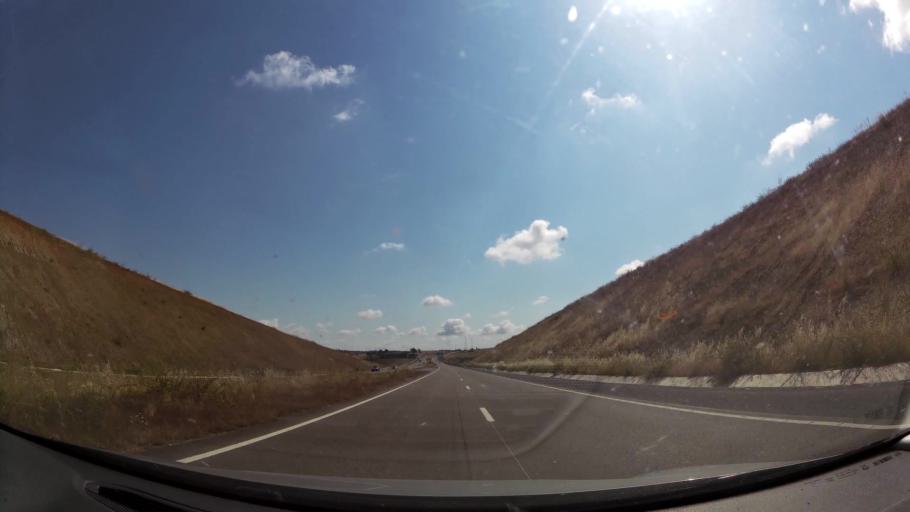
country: MA
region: Rabat-Sale-Zemmour-Zaer
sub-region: Skhirate-Temara
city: Temara
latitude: 33.8585
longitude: -6.8197
